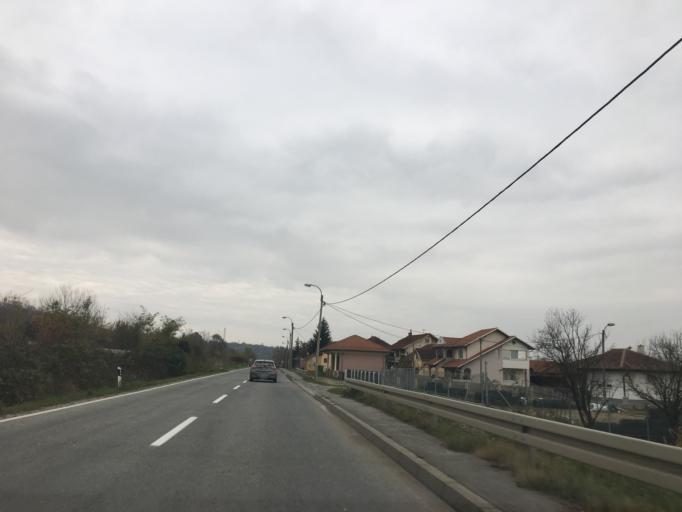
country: RS
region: Central Serbia
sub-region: Raski Okrug
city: Kraljevo
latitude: 43.7241
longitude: 20.7657
